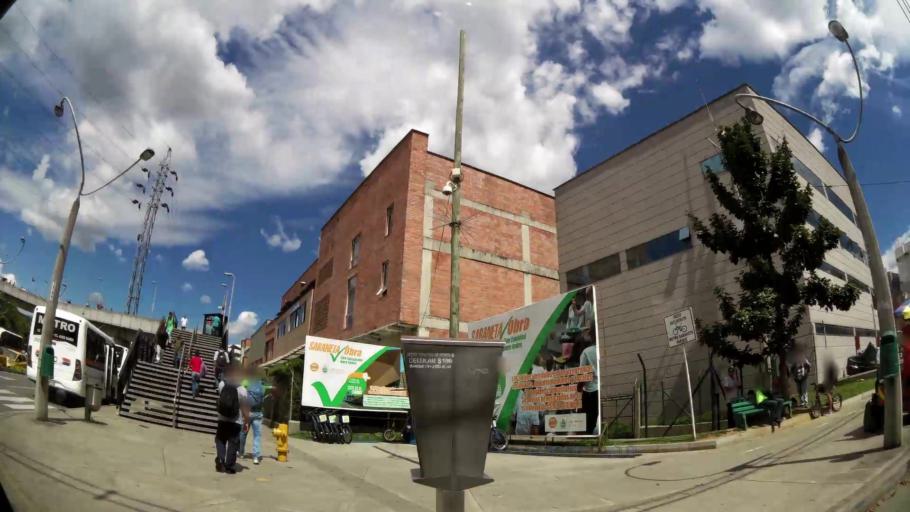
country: CO
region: Antioquia
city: Sabaneta
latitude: 6.1568
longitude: -75.6168
